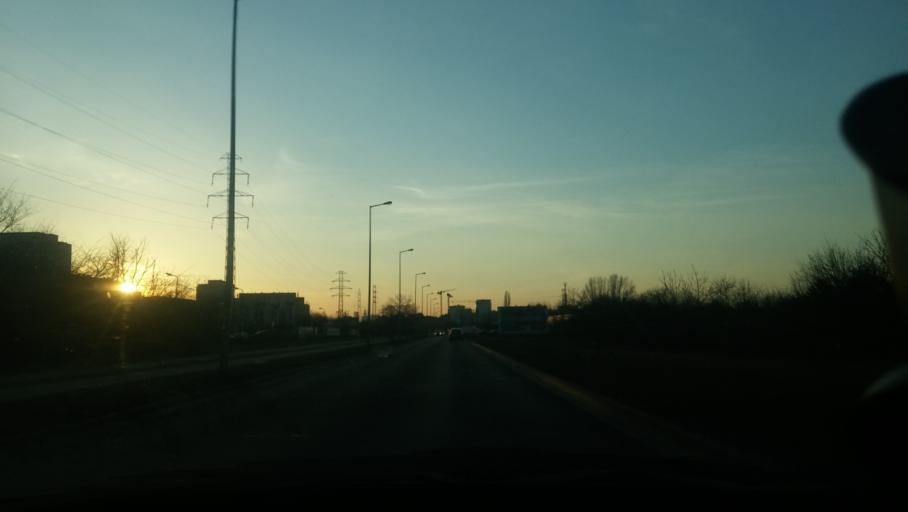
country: PL
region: Masovian Voivodeship
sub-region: Warszawa
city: Praga Poludnie
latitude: 52.2307
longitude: 21.1017
